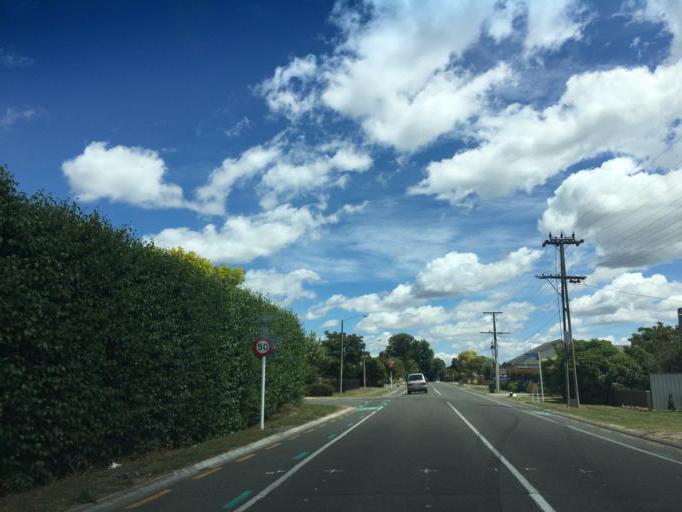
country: NZ
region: Hawke's Bay
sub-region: Hastings District
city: Hastings
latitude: -39.6519
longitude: 176.8673
